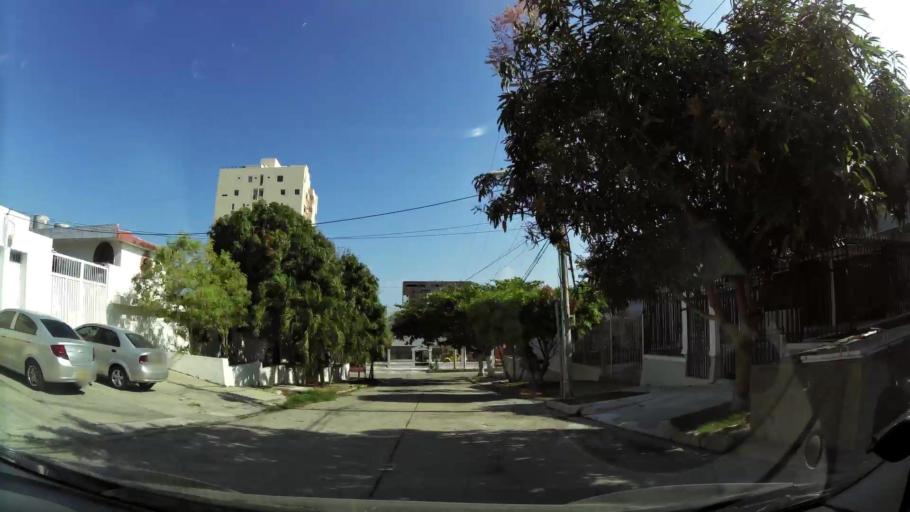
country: CO
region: Atlantico
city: Barranquilla
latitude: 10.9986
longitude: -74.8259
